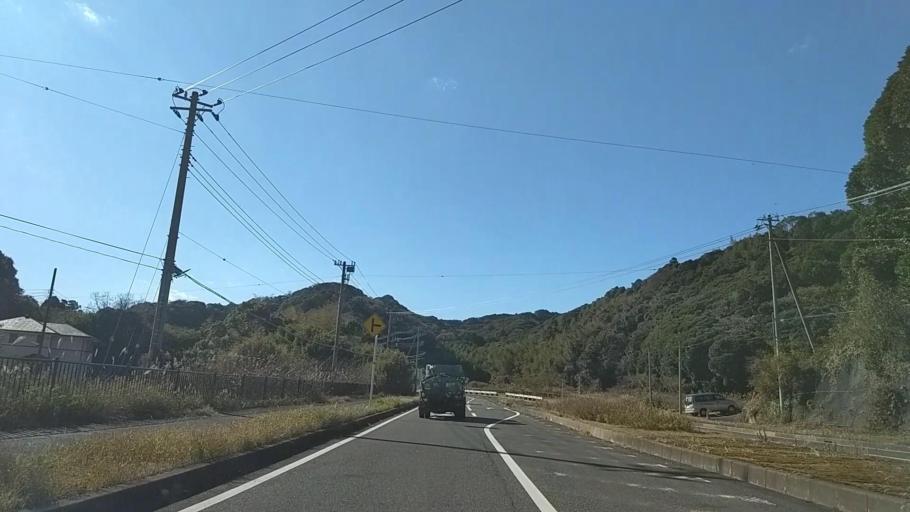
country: JP
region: Chiba
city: Tateyama
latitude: 34.9731
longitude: 139.8643
